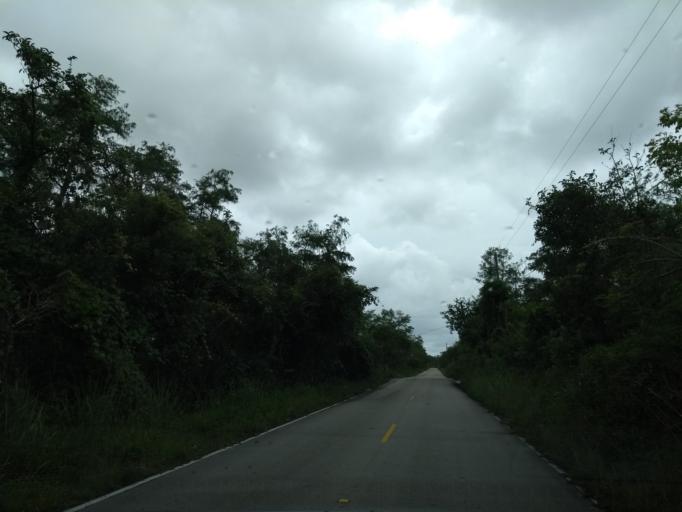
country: US
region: Florida
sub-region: Miami-Dade County
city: The Hammocks
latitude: 25.7593
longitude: -80.9265
